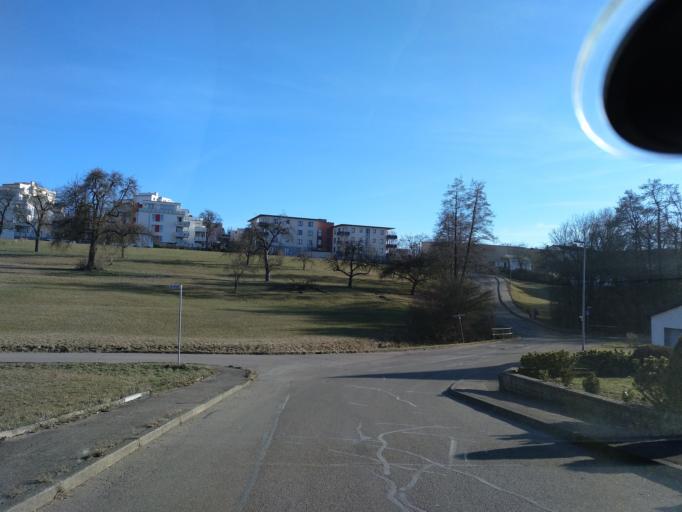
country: DE
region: Baden-Wuerttemberg
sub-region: Regierungsbezirk Stuttgart
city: Schwaebisch Hall
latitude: 49.1219
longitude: 9.7521
